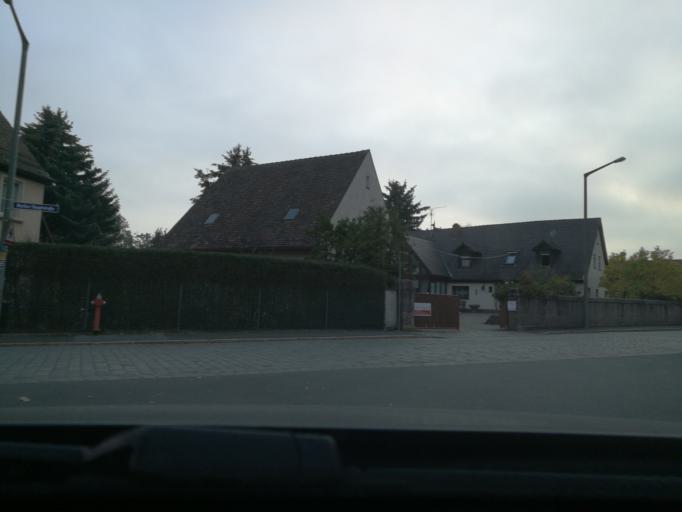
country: DE
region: Bavaria
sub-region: Regierungsbezirk Mittelfranken
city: Wetzendorf
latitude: 49.4969
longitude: 11.0455
